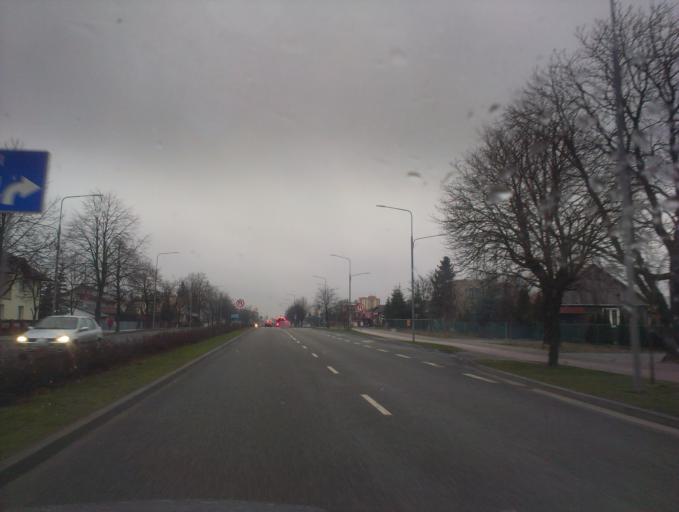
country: PL
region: Masovian Voivodeship
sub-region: Radom
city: Radom
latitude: 51.4235
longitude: 21.1513
